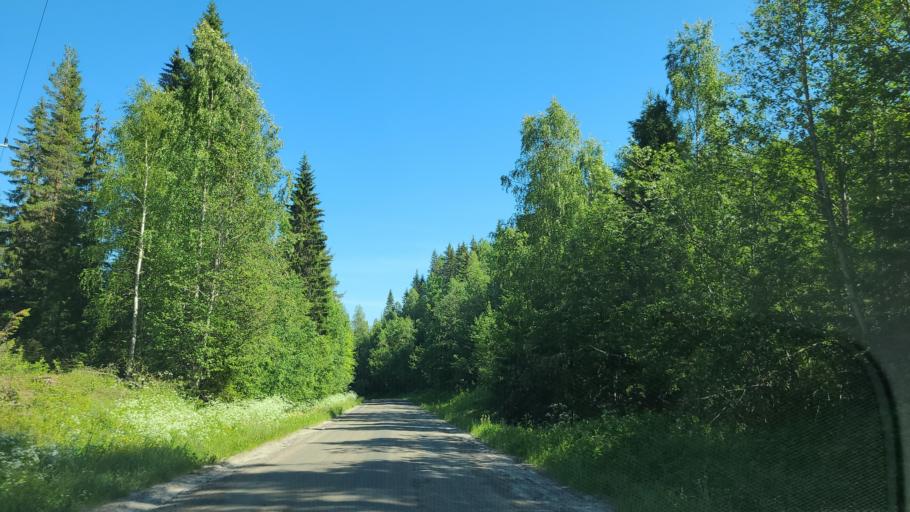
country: SE
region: Vaesterbotten
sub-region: Nordmalings Kommun
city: Nordmaling
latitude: 63.6466
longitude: 19.2336
